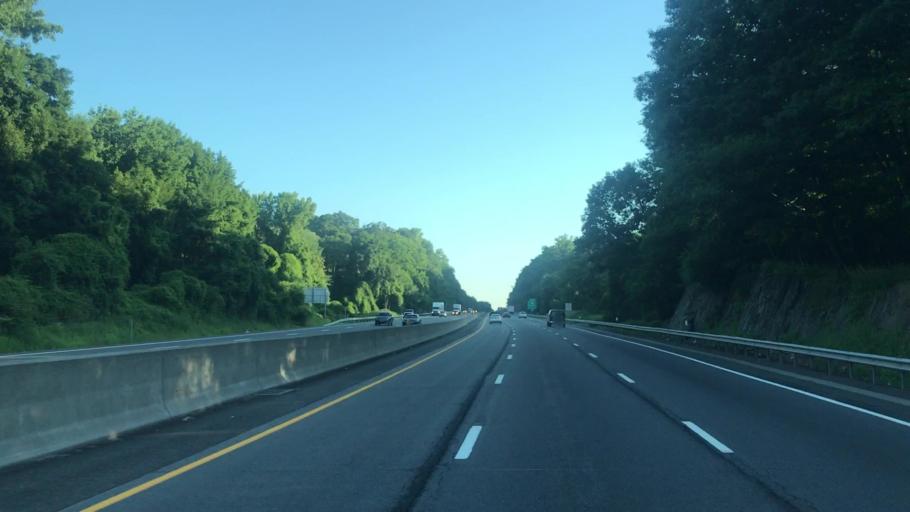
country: US
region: New York
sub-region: Westchester County
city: Ardsley
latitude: 40.9886
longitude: -73.8531
